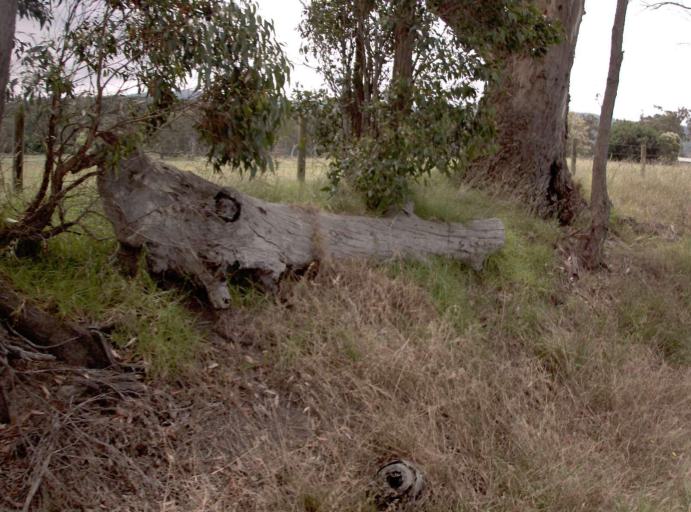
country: AU
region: Victoria
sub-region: Latrobe
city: Traralgon
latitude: -38.4893
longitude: 146.6801
